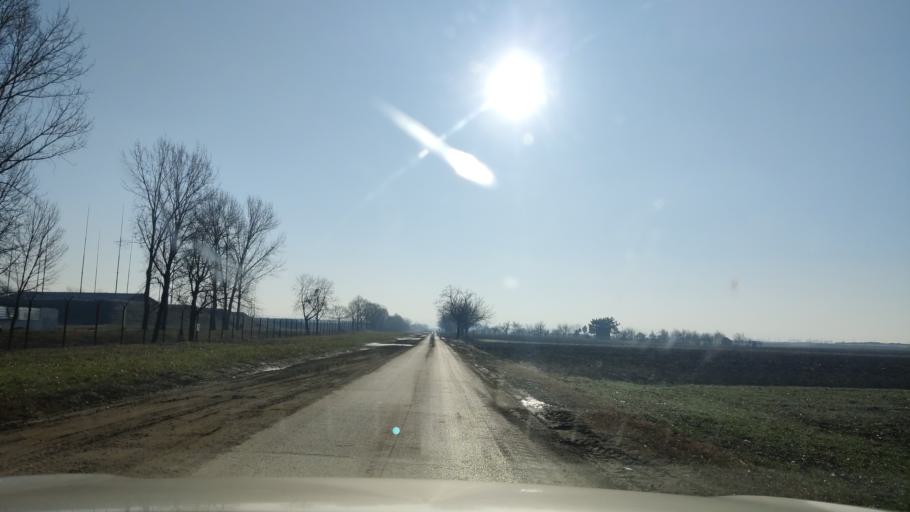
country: RS
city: Ostruznica
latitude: 44.7409
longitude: 20.2743
